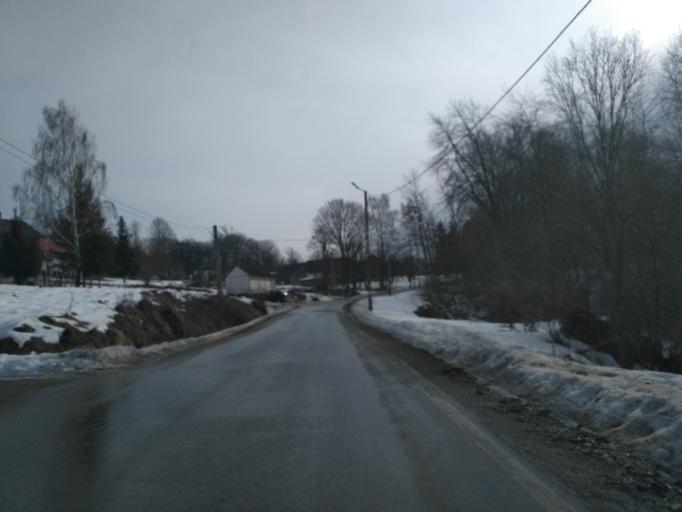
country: PL
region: Subcarpathian Voivodeship
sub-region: Powiat brzozowski
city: Dydnia
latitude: 49.6506
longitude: 22.1577
